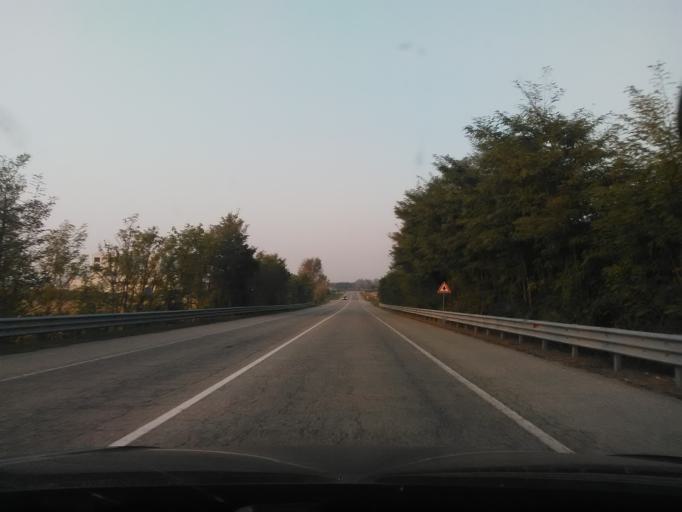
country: IT
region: Piedmont
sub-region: Provincia di Vercelli
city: Stroppiana
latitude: 45.2508
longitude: 8.4605
